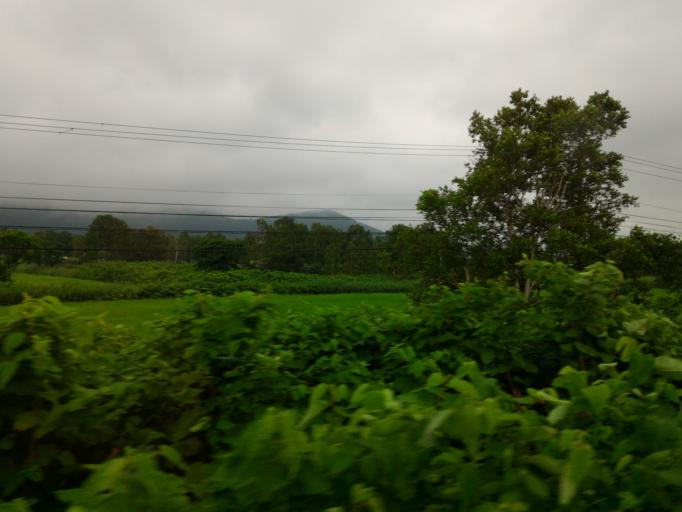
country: JP
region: Hokkaido
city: Makubetsu
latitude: 44.8992
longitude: 141.9404
